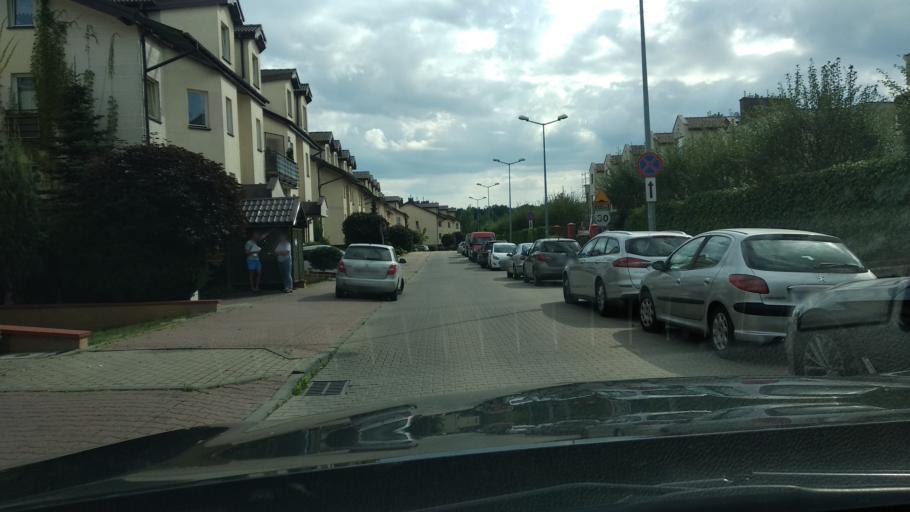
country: PL
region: Masovian Voivodeship
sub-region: Warszawa
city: Ursynow
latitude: 52.1343
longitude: 21.0489
